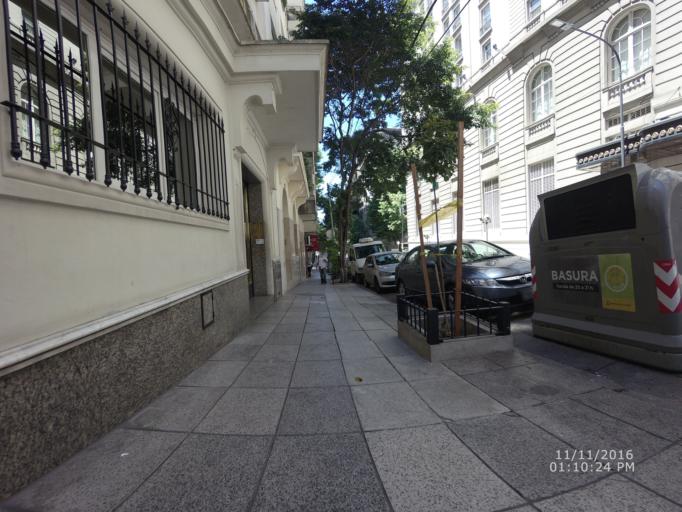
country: AR
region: Buenos Aires F.D.
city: Retiro
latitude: -34.5873
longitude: -58.3887
